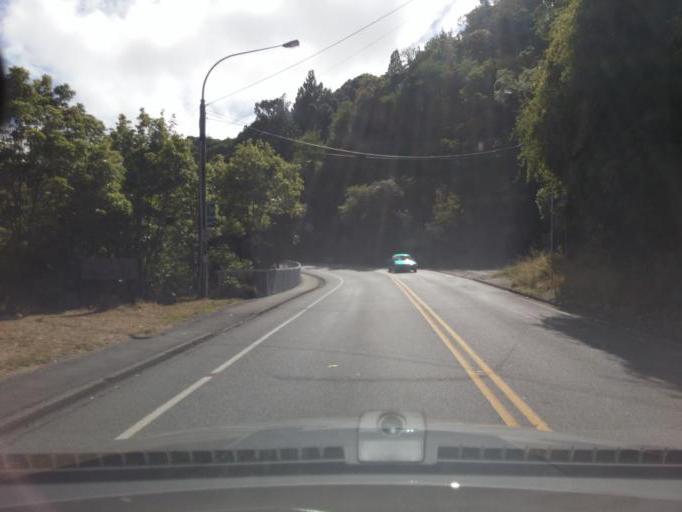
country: NZ
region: Wellington
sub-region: Wellington City
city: Kelburn
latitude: -41.2564
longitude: 174.7784
